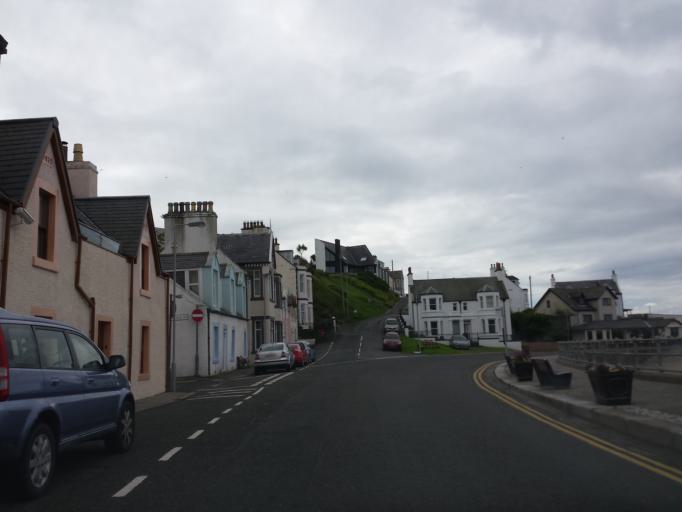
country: GB
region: Scotland
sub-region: Dumfries and Galloway
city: Stranraer
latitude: 54.8414
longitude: -5.1165
